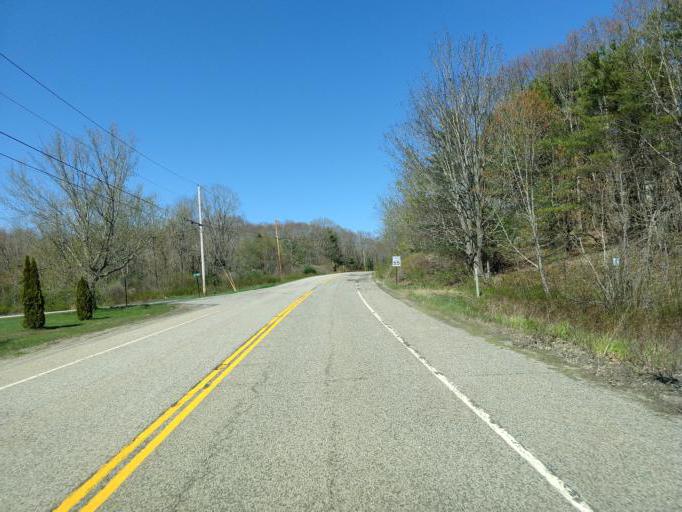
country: US
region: Maine
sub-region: York County
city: Arundel
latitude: 43.4214
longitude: -70.4070
